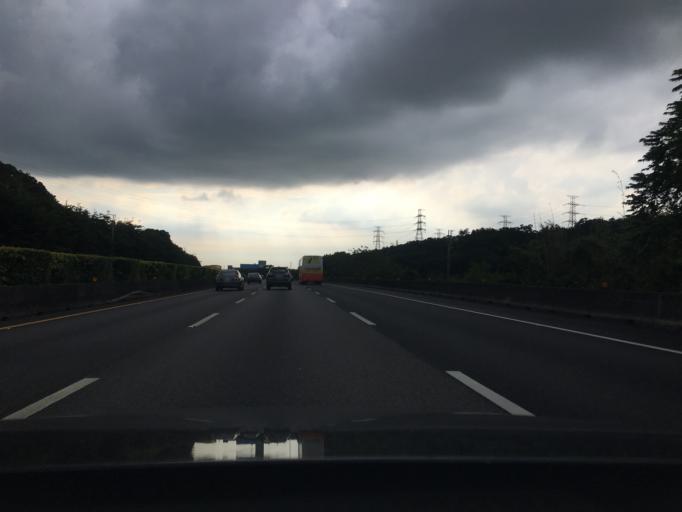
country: TW
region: Taiwan
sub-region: Hsinchu
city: Zhubei
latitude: 24.8932
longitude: 121.1068
